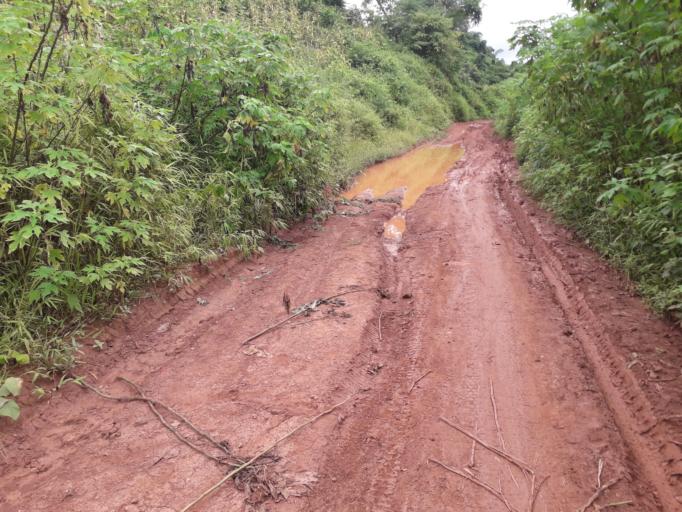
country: CN
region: Yunnan
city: Menglie
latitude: 22.2007
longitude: 101.6778
